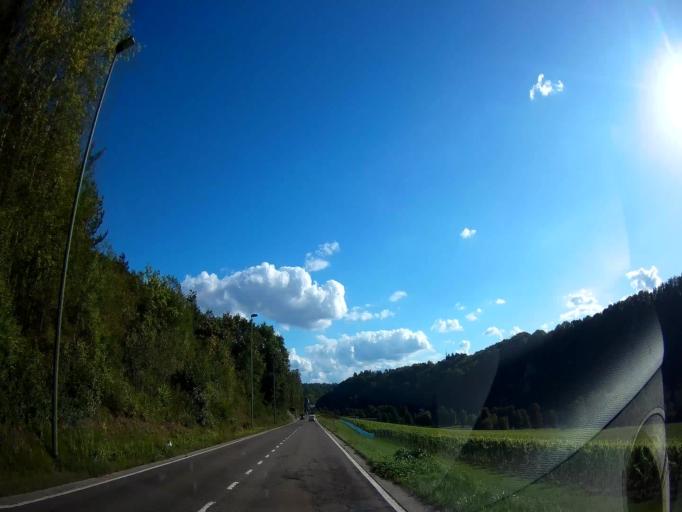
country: BE
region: Wallonia
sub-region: Province de Namur
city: Dinant
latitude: 50.2849
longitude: 4.8965
